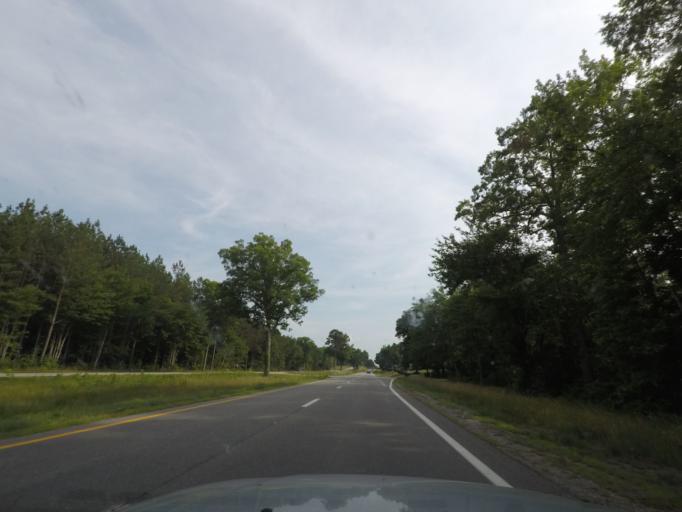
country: US
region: Virginia
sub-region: Mecklenburg County
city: Chase City
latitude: 36.9628
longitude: -78.4949
